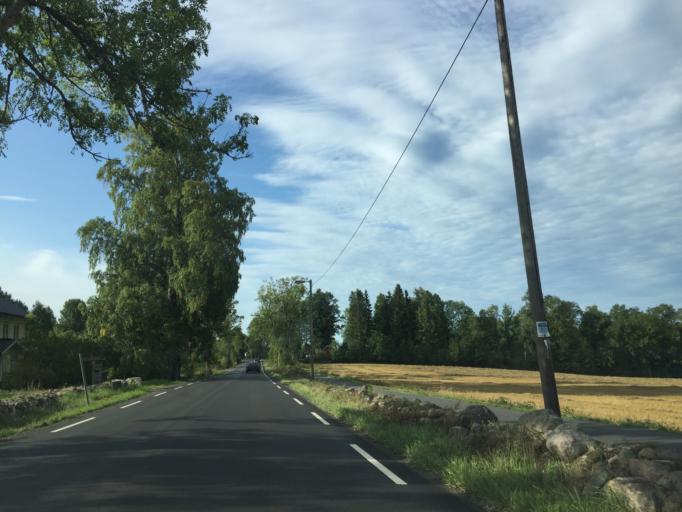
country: NO
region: Akershus
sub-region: As
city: As
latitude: 59.7125
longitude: 10.7731
